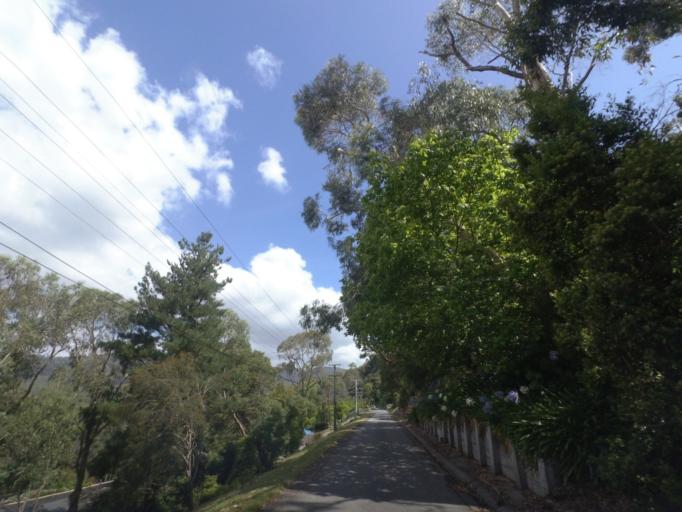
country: AU
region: Victoria
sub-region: Yarra Ranges
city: Mount Evelyn
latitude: -37.7918
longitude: 145.3587
